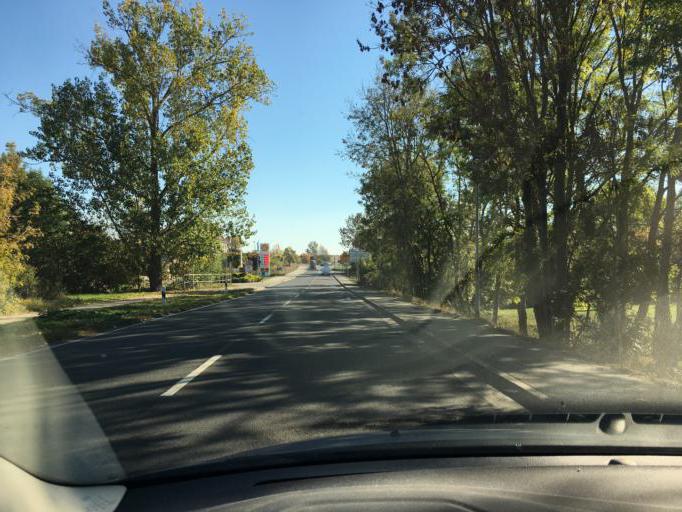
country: DE
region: Saxony-Anhalt
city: Wanzleben
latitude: 52.0562
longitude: 11.4490
